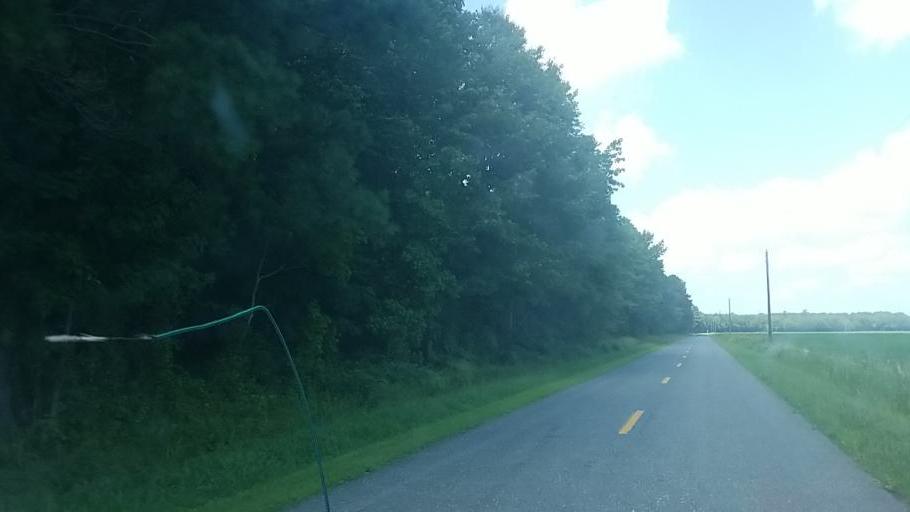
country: US
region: Maryland
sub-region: Dorchester County
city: Hurlock
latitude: 38.4638
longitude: -75.8462
